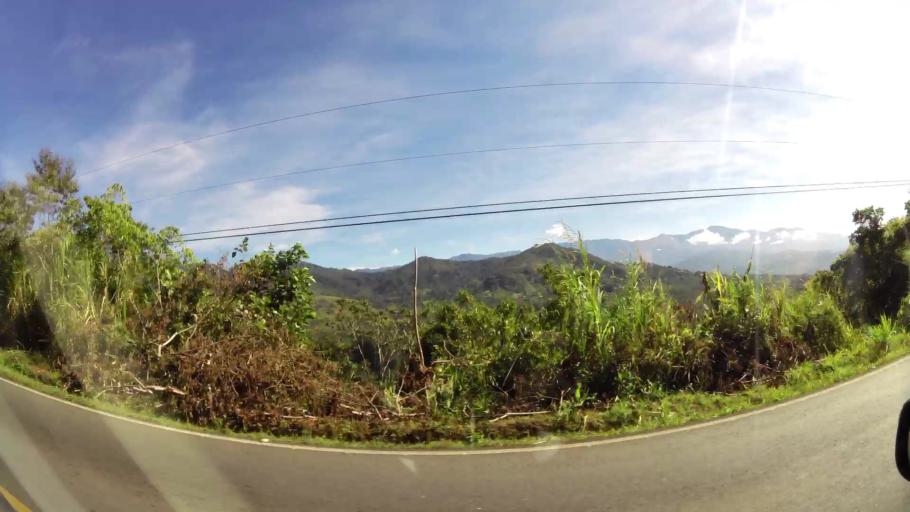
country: CR
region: San Jose
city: San Isidro
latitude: 9.4221
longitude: -83.7110
